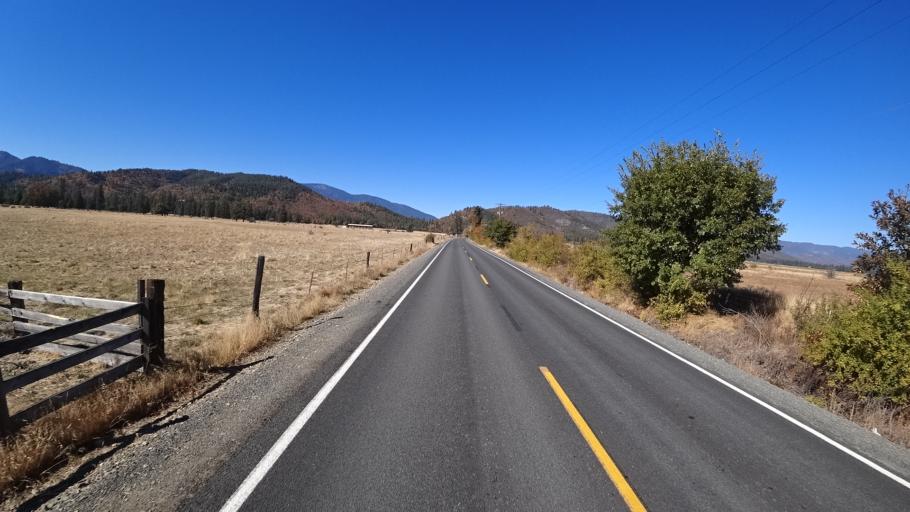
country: US
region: California
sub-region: Siskiyou County
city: Yreka
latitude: 41.5540
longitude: -122.9182
